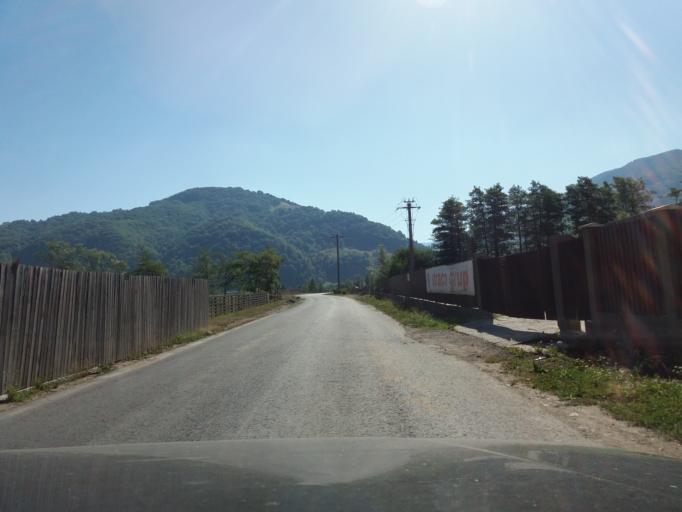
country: RO
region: Hunedoara
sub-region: Oras Petrila
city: Petrila
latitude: 45.4206
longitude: 23.4201
